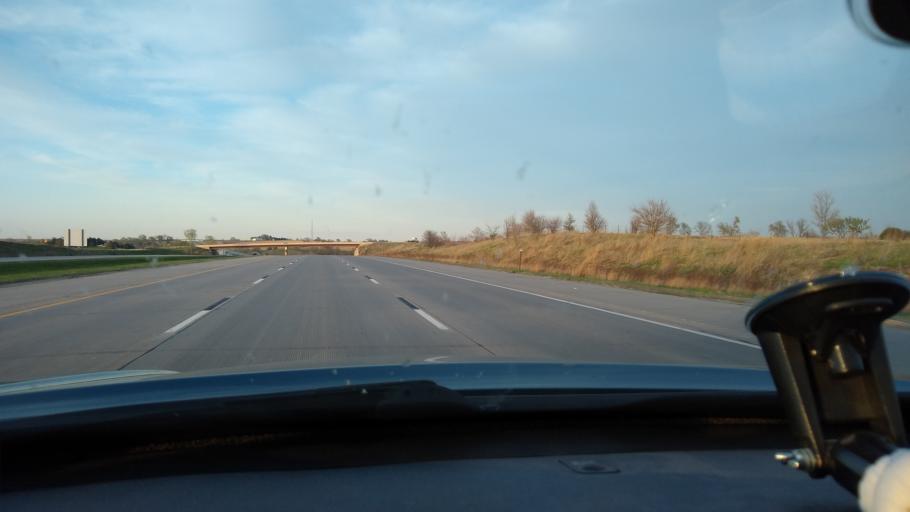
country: US
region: Nebraska
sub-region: Sarpy County
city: Gretna
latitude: 41.1020
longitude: -96.2382
